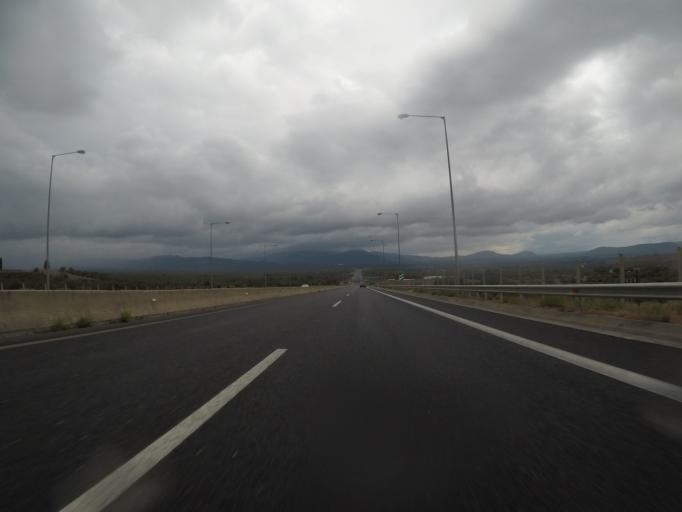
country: GR
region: Peloponnese
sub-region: Nomos Arkadias
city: Megalopoli
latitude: 37.3864
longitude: 22.1686
